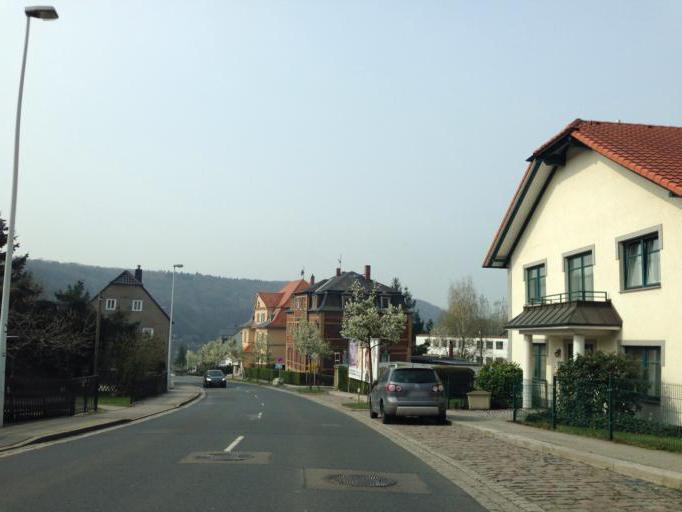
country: DE
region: Saxony
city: Freital
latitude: 51.0026
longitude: 13.6797
